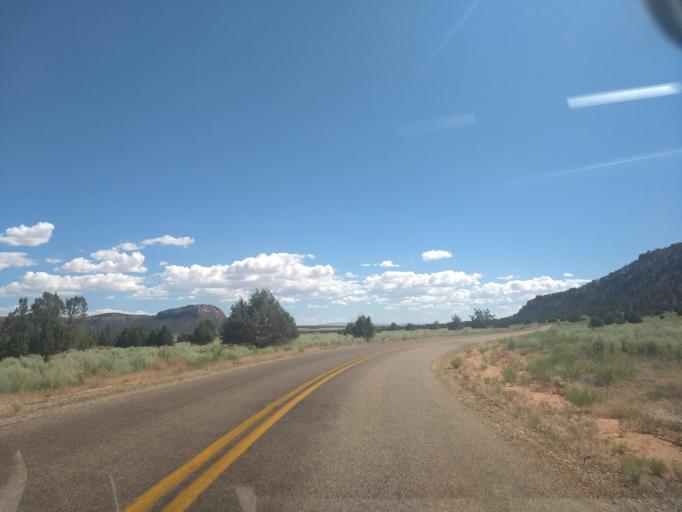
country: US
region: Utah
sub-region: Washington County
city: Hildale
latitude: 36.9653
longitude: -112.8705
